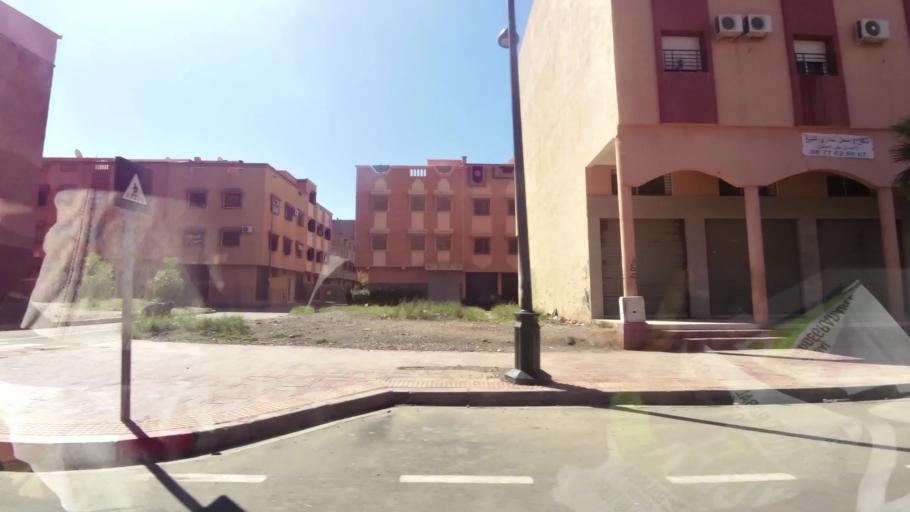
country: MA
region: Marrakech-Tensift-Al Haouz
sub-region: Marrakech
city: Marrakesh
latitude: 31.5946
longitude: -8.0403
